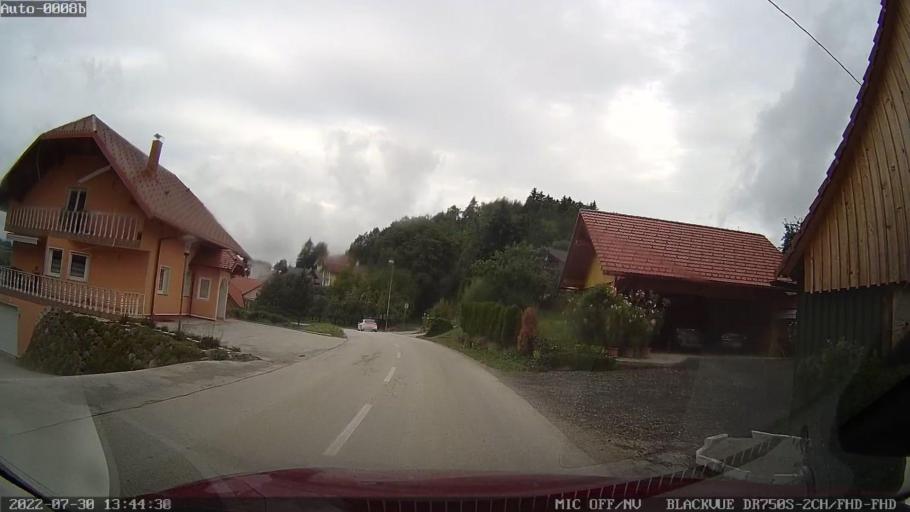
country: SI
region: Ivancna Gorica
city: Sentvid pri Sticni
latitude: 45.9179
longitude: 14.8917
